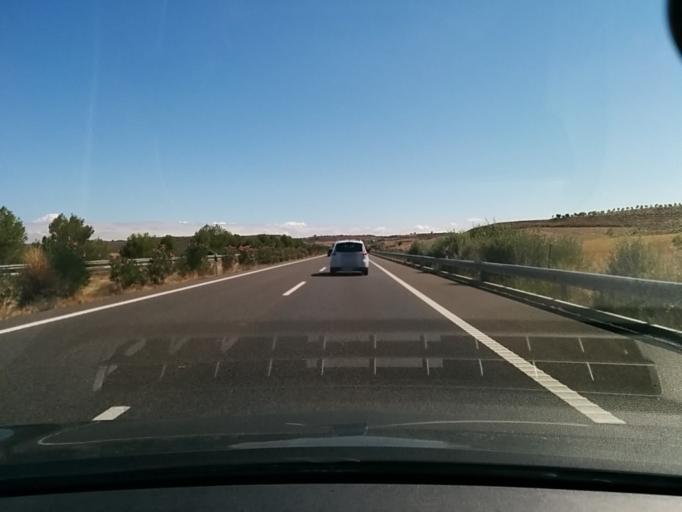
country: ES
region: Aragon
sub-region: Provincia de Huesca
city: Almudebar
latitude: 42.0490
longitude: -0.5555
